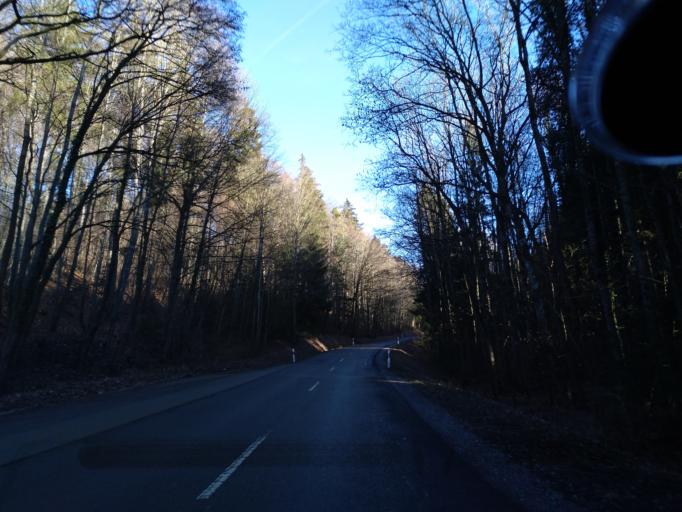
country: DE
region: Baden-Wuerttemberg
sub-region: Regierungsbezirk Stuttgart
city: Obersontheim
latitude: 49.0883
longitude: 9.9258
